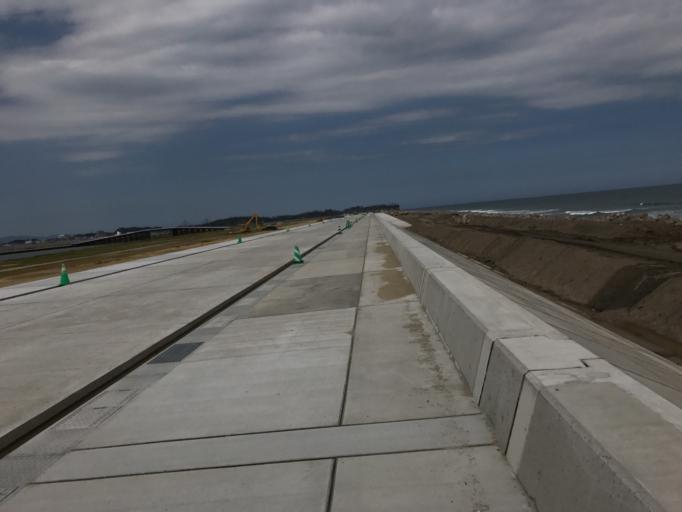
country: JP
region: Miyagi
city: Marumori
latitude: 37.8003
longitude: 140.9859
